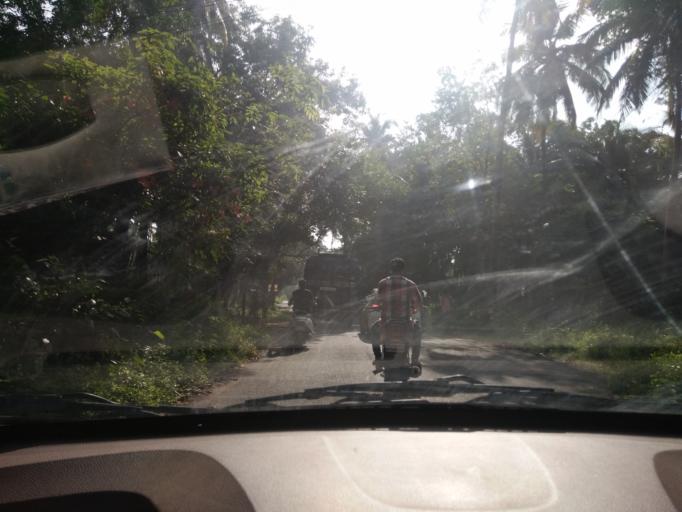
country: IN
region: Goa
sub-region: South Goa
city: Benaulim
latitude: 15.2619
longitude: 73.9372
